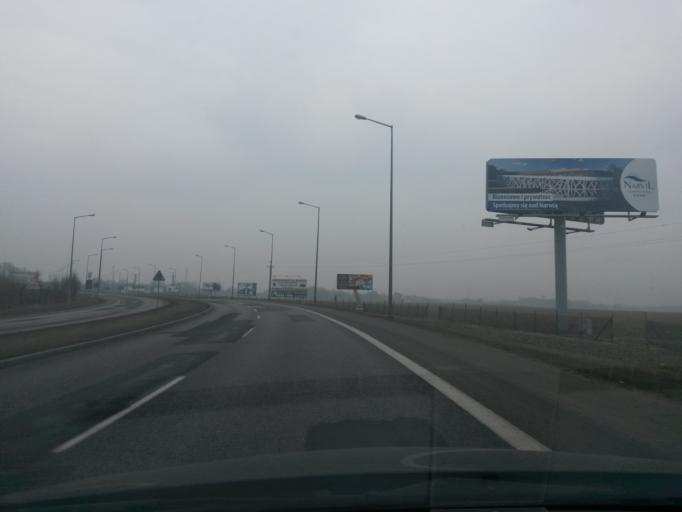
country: PL
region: Masovian Voivodeship
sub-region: Powiat legionowski
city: Bialobrzegi
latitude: 52.4671
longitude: 21.0299
